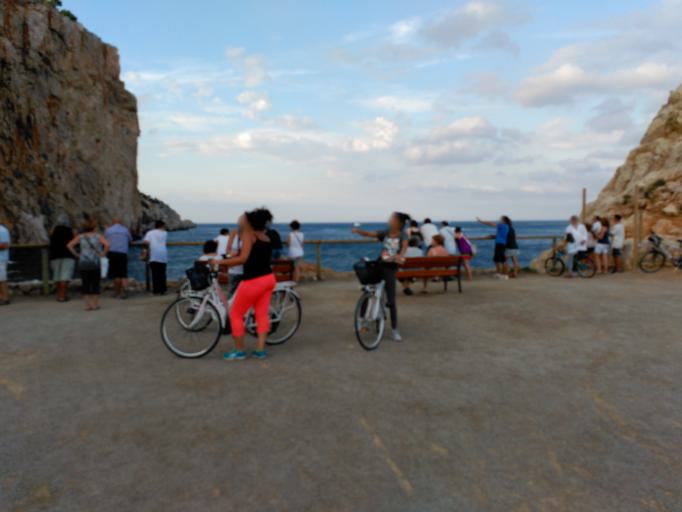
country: ES
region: Catalonia
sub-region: Provincia de Girona
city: Torroella de Montgri
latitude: 42.0540
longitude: 3.2111
